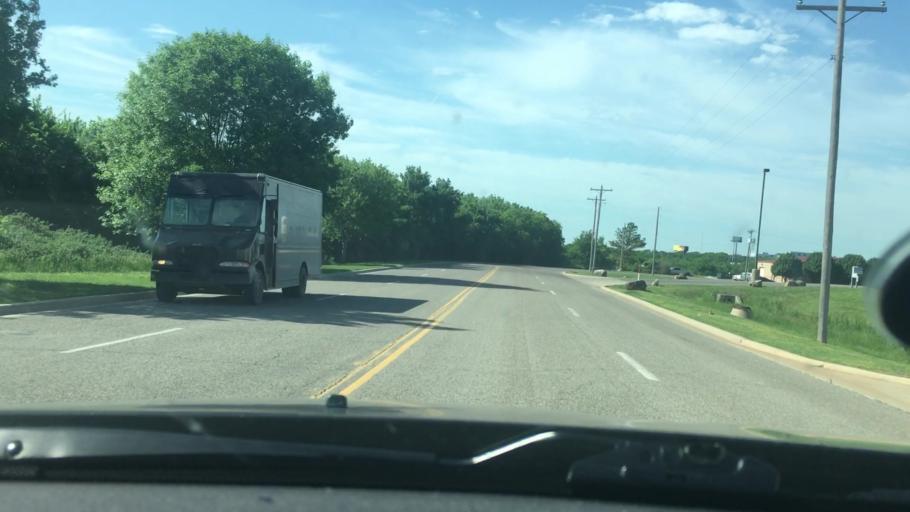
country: US
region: Oklahoma
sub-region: Carter County
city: Ardmore
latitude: 34.1952
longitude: -97.1673
